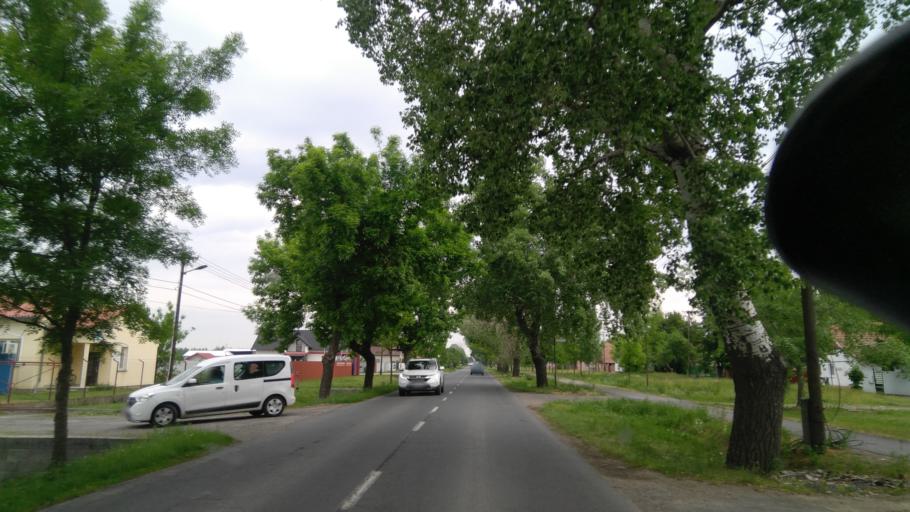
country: HU
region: Bekes
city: Veszto
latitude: 46.9015
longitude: 21.2528
